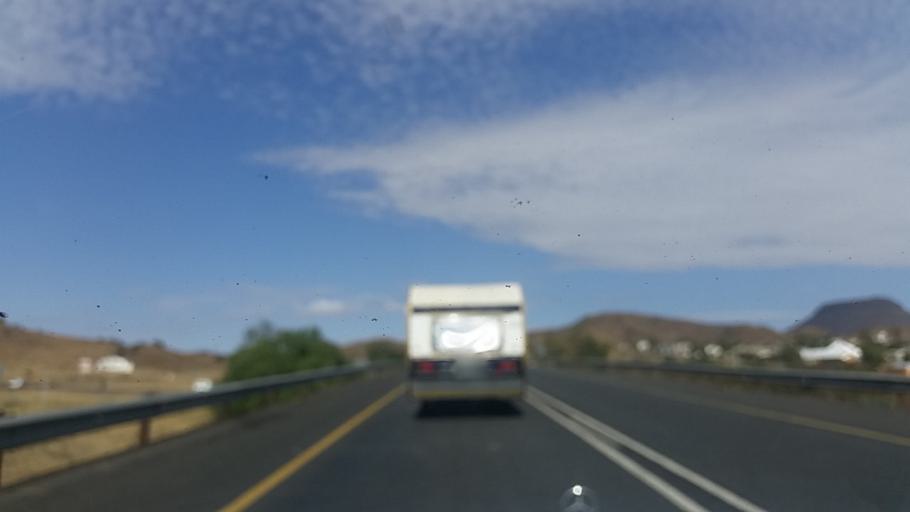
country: ZA
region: Northern Cape
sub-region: Pixley ka Seme District Municipality
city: Colesberg
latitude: -30.7092
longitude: 25.1064
